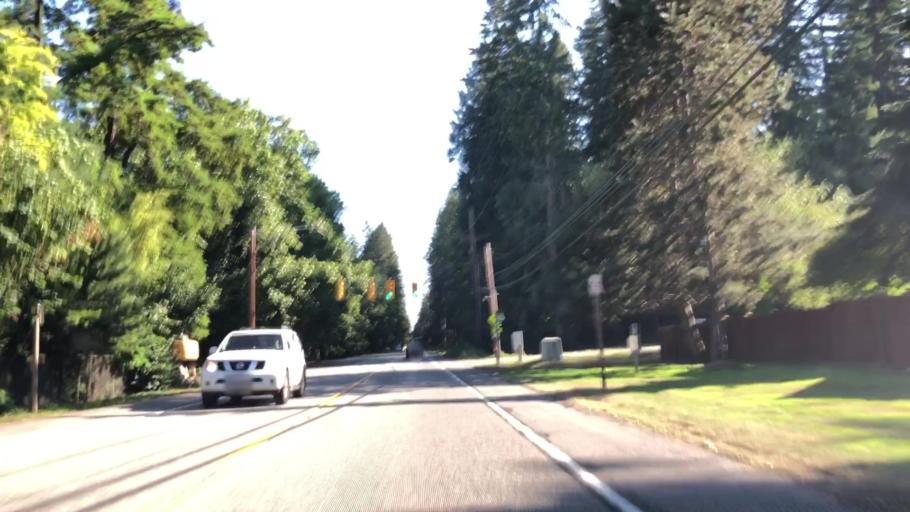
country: US
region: Washington
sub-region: King County
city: Cottage Lake
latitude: 47.7457
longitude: -122.0747
